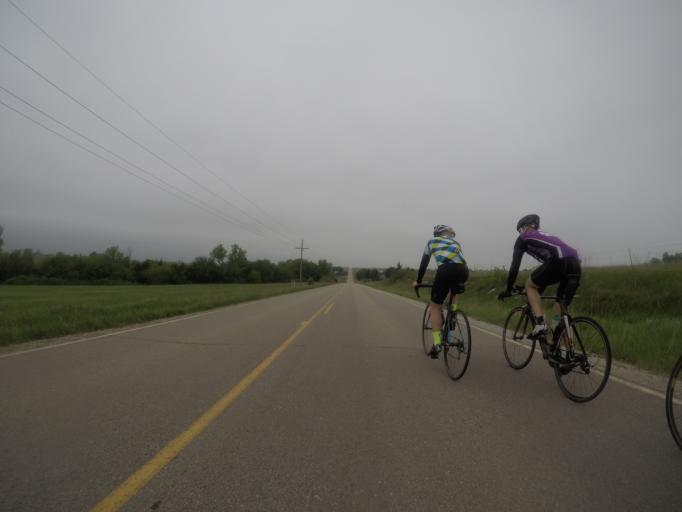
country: US
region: Kansas
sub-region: Pottawatomie County
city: Westmoreland
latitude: 39.5129
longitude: -96.3141
